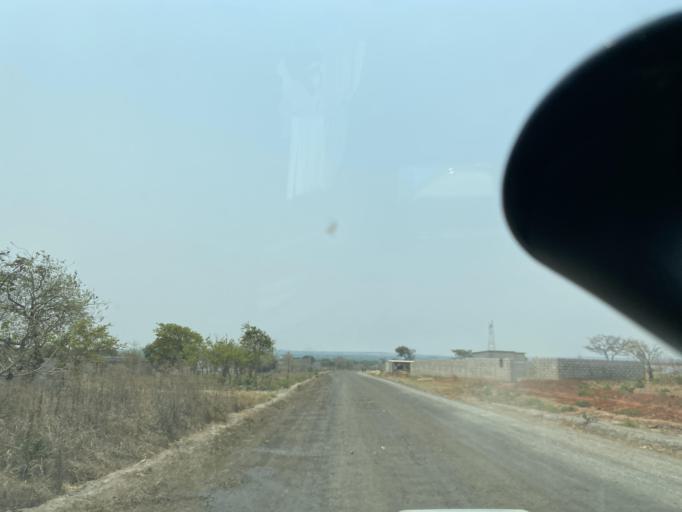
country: ZM
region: Lusaka
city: Lusaka
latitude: -15.5441
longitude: 28.4454
